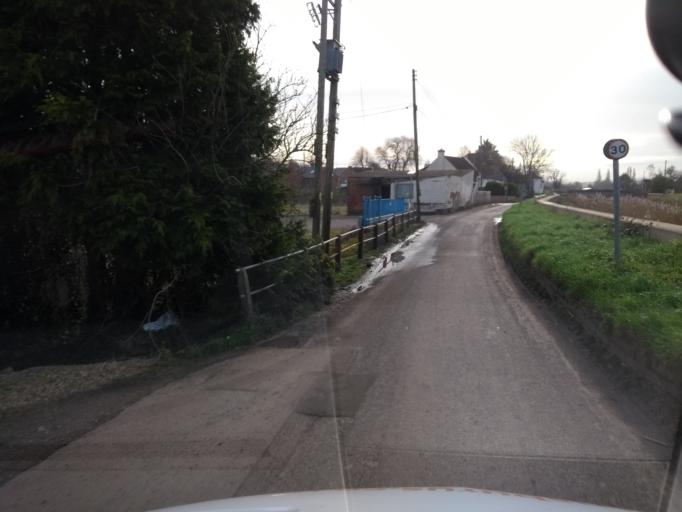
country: GB
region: England
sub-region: Somerset
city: Westonzoyland
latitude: 51.0711
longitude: -2.9197
